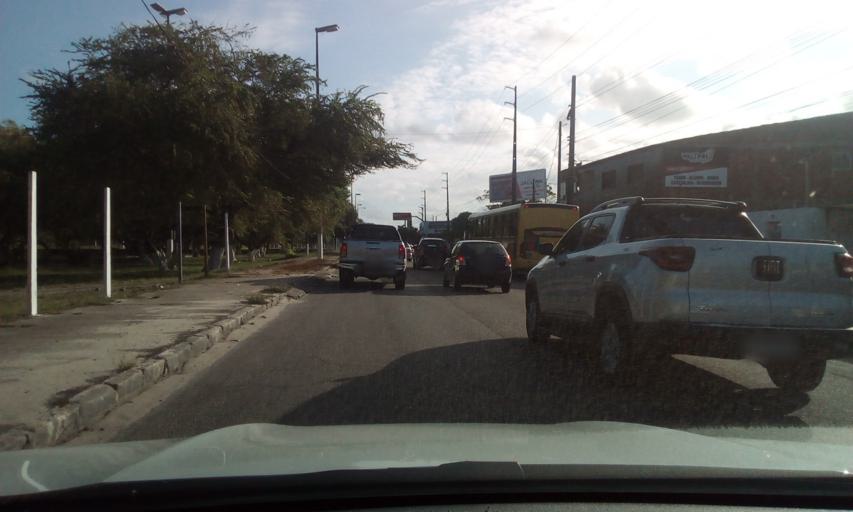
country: BR
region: Pernambuco
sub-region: Olinda
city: Olinda
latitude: -8.0292
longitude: -34.8661
